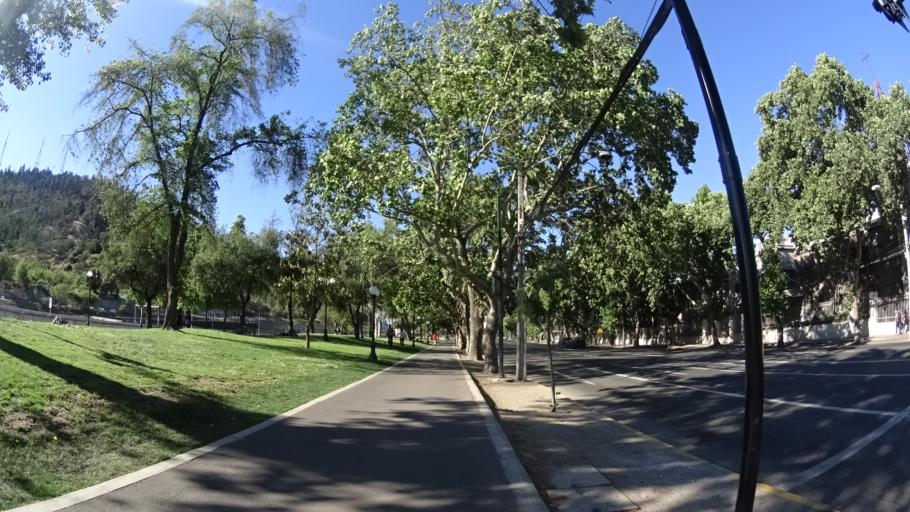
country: CL
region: Santiago Metropolitan
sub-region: Provincia de Santiago
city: Santiago
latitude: -33.4275
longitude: -70.6226
